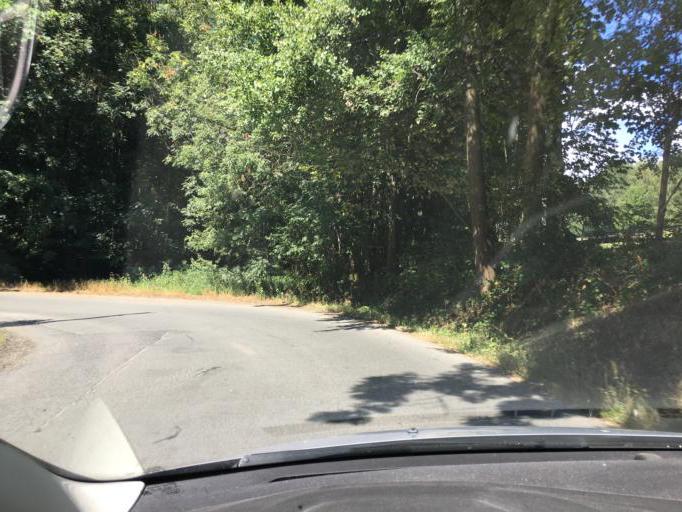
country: CZ
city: Plavy
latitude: 50.7036
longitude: 15.3485
